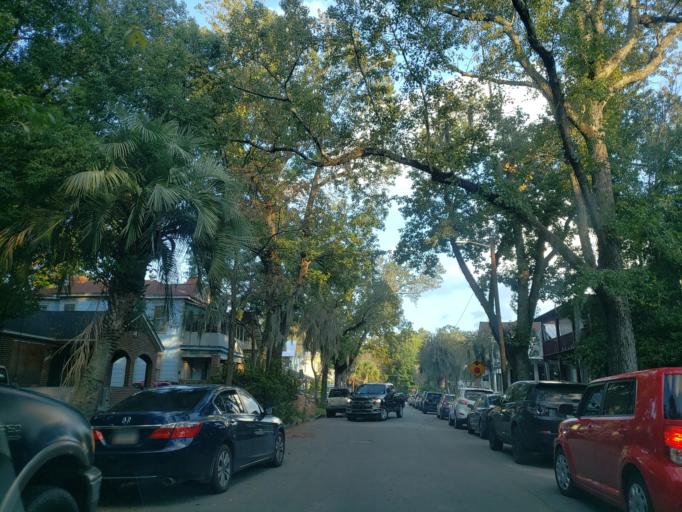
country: US
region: Georgia
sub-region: Chatham County
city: Savannah
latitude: 32.0557
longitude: -81.0821
